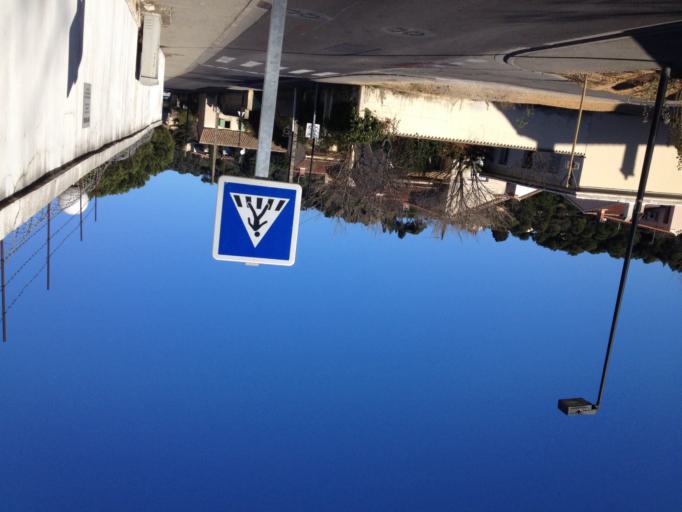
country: FR
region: Provence-Alpes-Cote d'Azur
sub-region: Departement du Vaucluse
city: Orange
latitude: 44.1289
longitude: 4.8144
